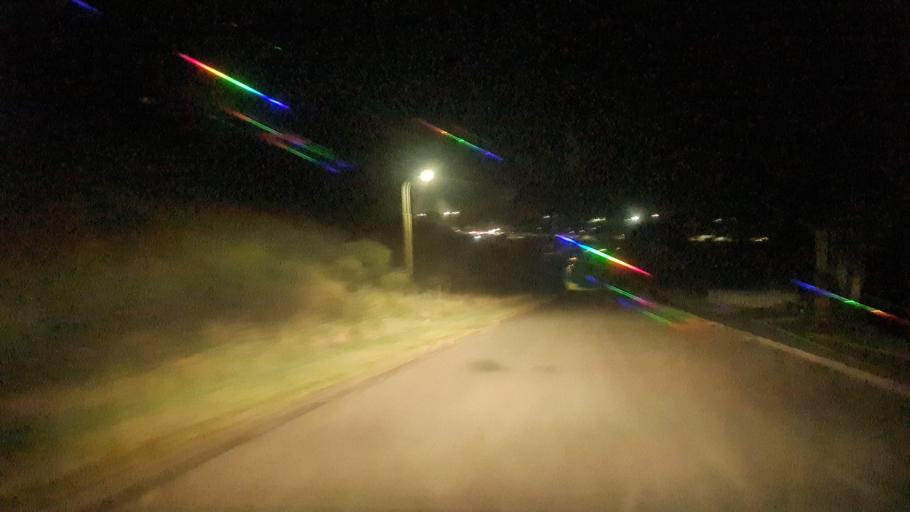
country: NZ
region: Otago
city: Oamaru
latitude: -45.0790
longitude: 170.9723
